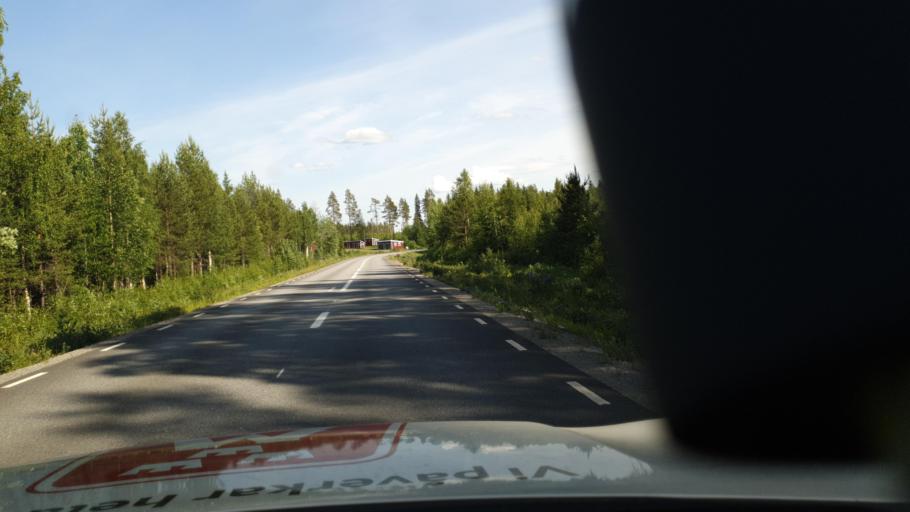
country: SE
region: Vaesterbotten
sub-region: Skelleftea Kommun
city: Boliden
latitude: 64.7397
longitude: 20.3707
